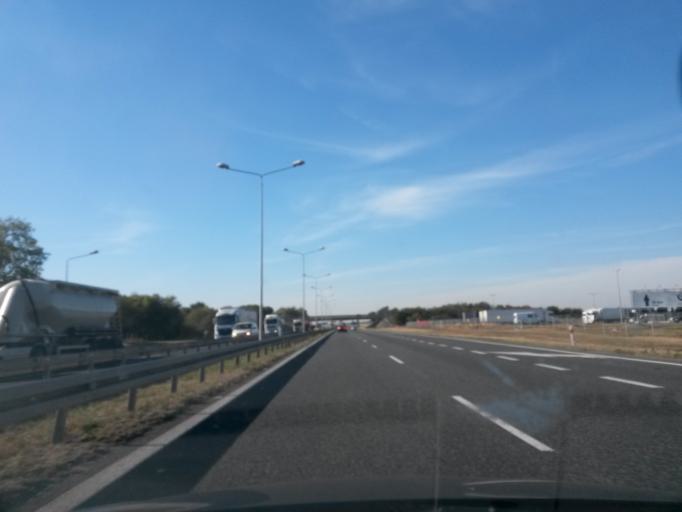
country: PL
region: Opole Voivodeship
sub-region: Powiat brzeski
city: Grodkow
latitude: 50.7823
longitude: 17.3481
